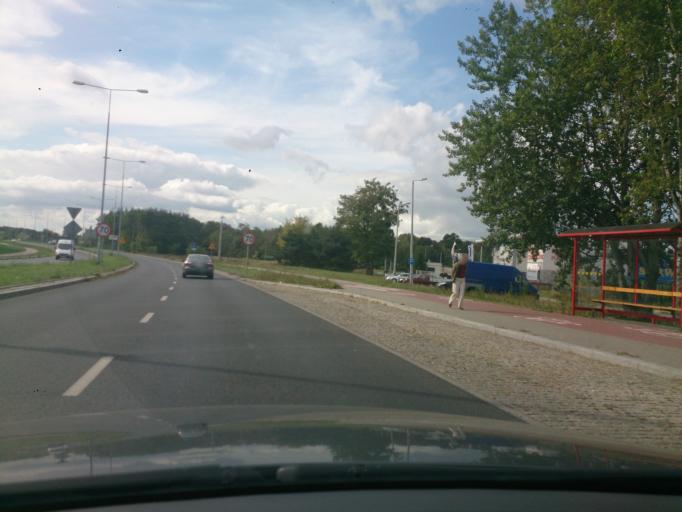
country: PL
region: Kujawsko-Pomorskie
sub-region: Grudziadz
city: Grudziadz
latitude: 53.4669
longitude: 18.7523
